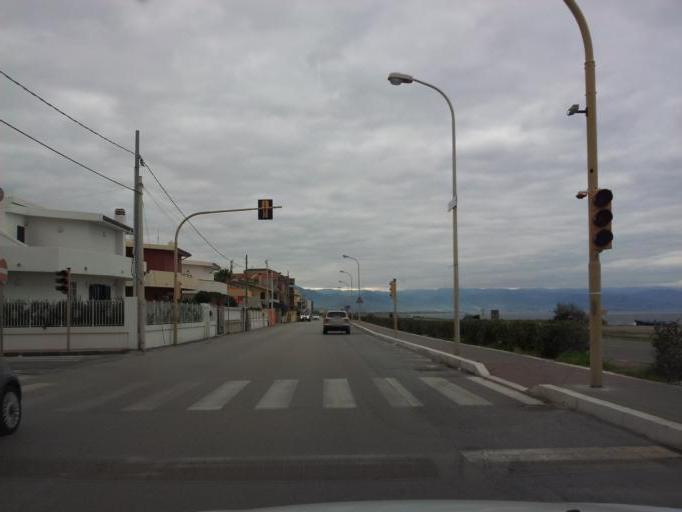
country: IT
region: Sicily
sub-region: Messina
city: Milazzo
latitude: 38.2132
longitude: 15.2307
